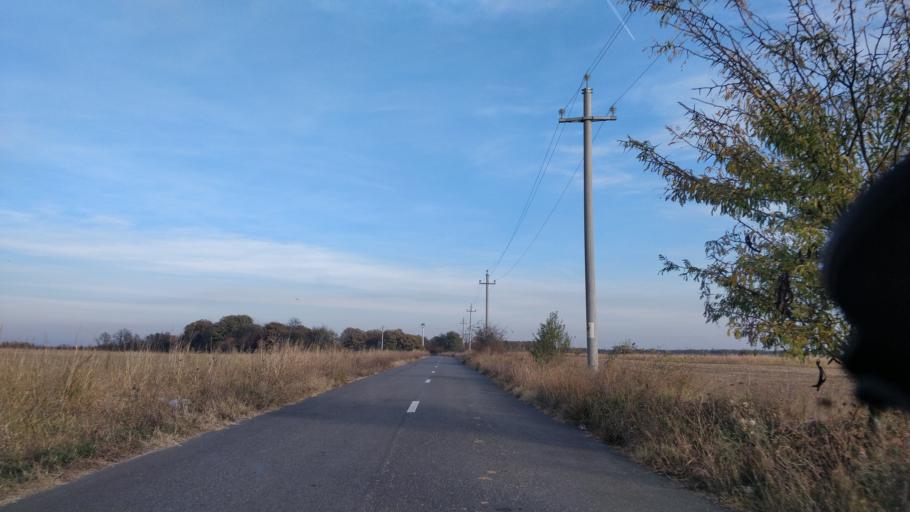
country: RO
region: Giurgiu
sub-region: Comuna Bucsani
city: Bucsani
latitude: 44.3357
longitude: 25.6505
